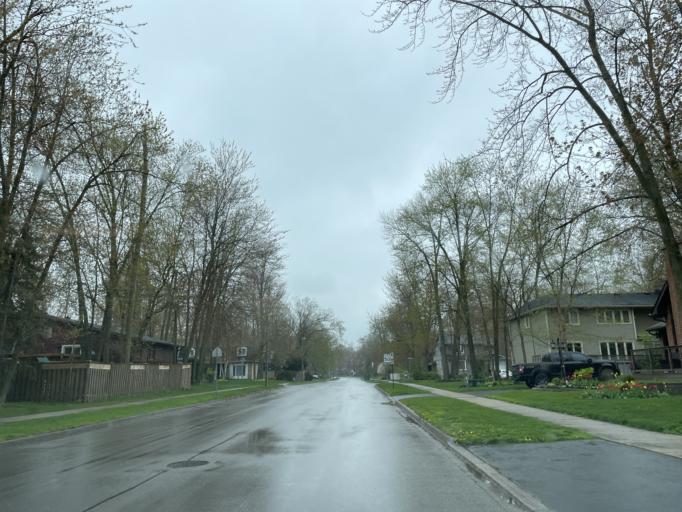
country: CA
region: Ontario
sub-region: Wellington County
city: Guelph
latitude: 43.5343
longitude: -80.2898
